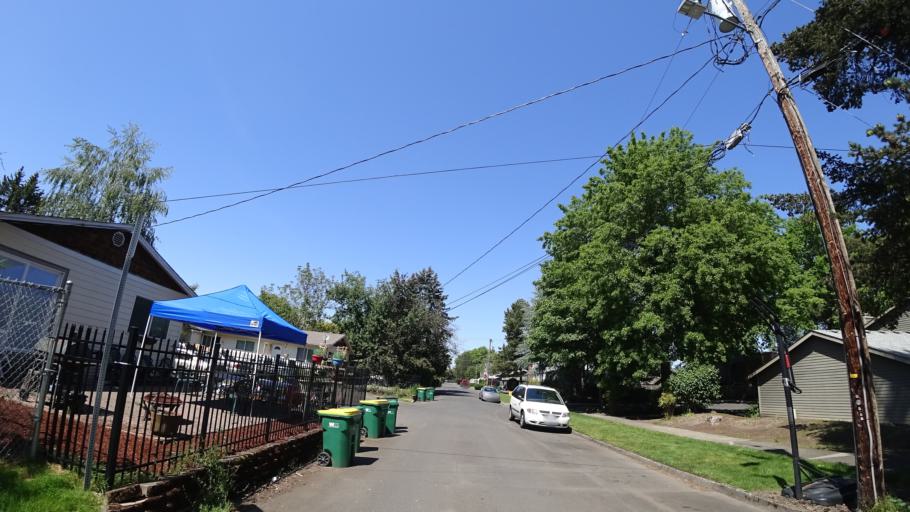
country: US
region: Oregon
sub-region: Washington County
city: Beaverton
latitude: 45.4837
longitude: -122.7995
